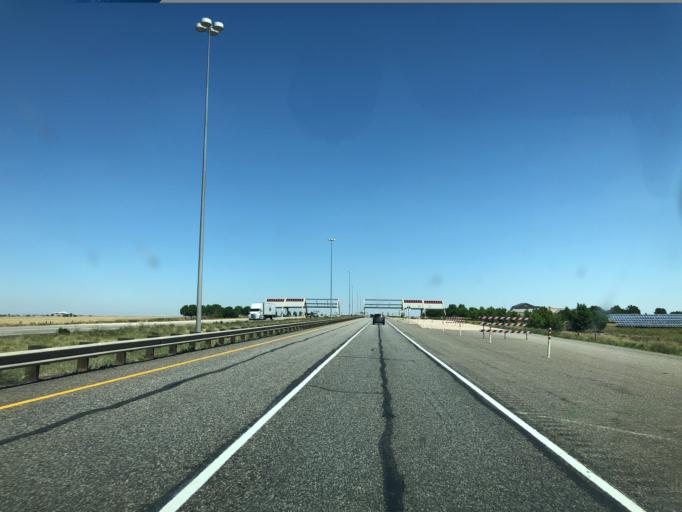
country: US
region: Colorado
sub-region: Adams County
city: Aurora
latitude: 39.7675
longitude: -104.7164
